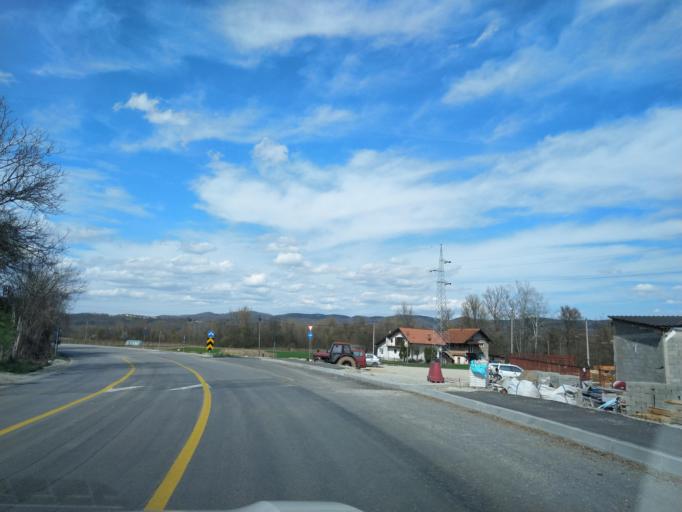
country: RS
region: Central Serbia
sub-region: Zlatiborski Okrug
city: Arilje
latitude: 43.7848
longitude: 20.1087
